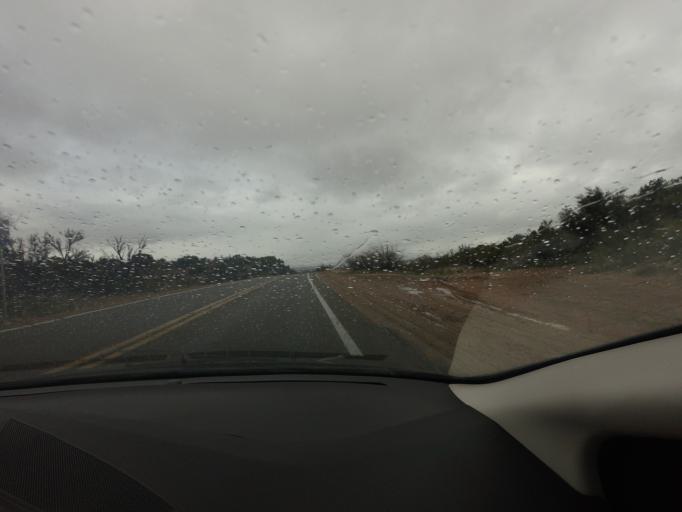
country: US
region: Arizona
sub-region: Yavapai County
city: Cornville
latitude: 34.6975
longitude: -111.8590
